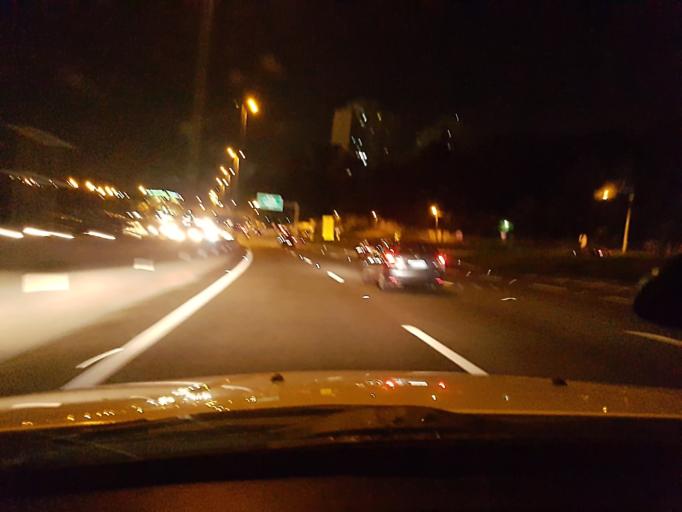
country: BR
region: Sao Paulo
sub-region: Taboao Da Serra
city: Taboao da Serra
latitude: -23.5864
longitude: -46.7486
